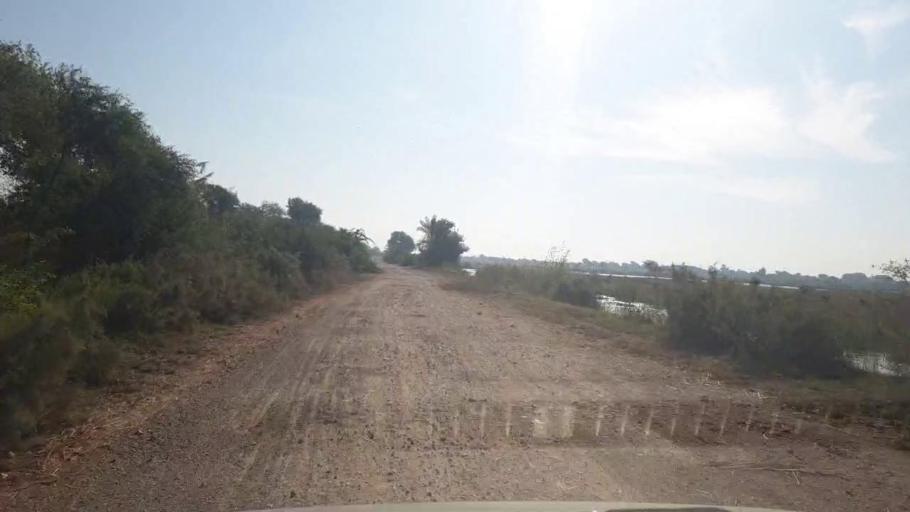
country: PK
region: Sindh
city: Rajo Khanani
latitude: 24.9766
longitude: 68.7794
